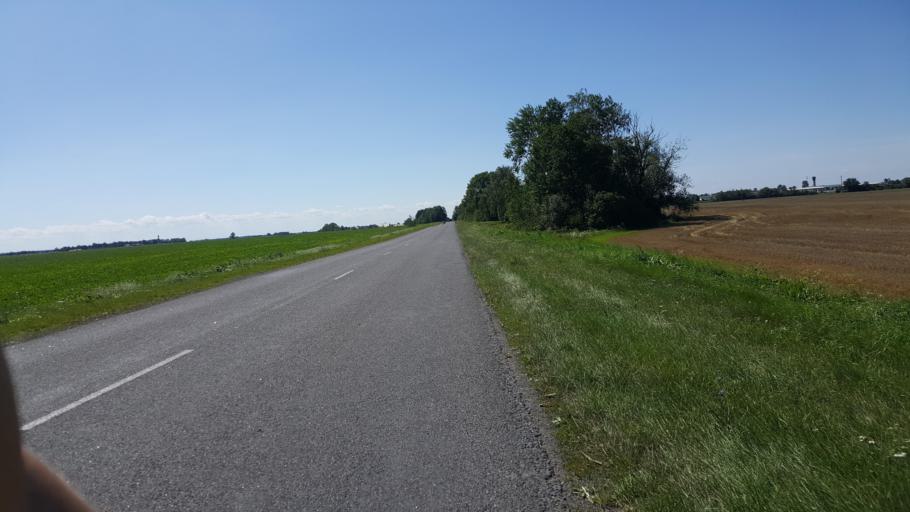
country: BY
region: Brest
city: Charnawchytsy
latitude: 52.2054
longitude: 23.7780
